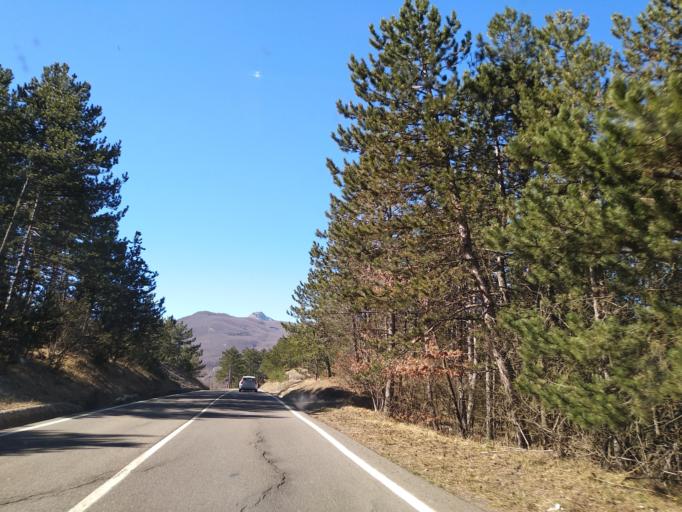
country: IT
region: Emilia-Romagna
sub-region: Provincia di Reggio Emilia
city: Busana
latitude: 44.4094
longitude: 10.3432
